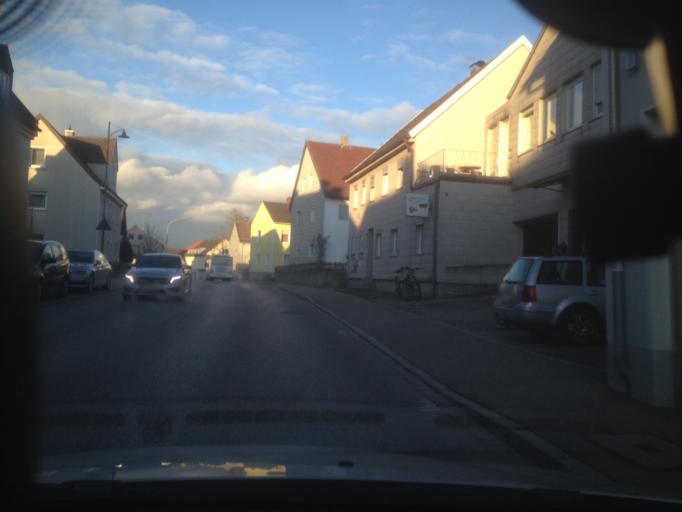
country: DE
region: Bavaria
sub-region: Swabia
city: Mering
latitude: 48.2698
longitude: 10.9872
